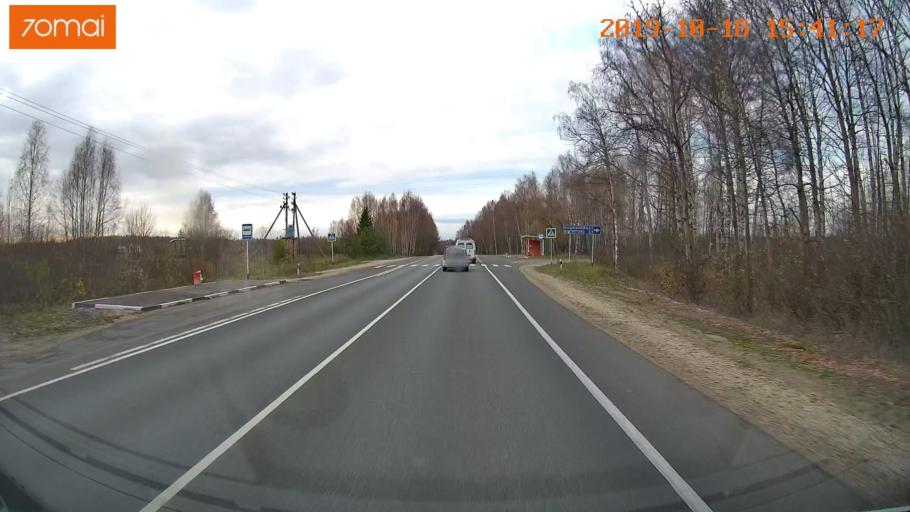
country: RU
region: Vladimir
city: Golovino
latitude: 55.9438
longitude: 40.5850
